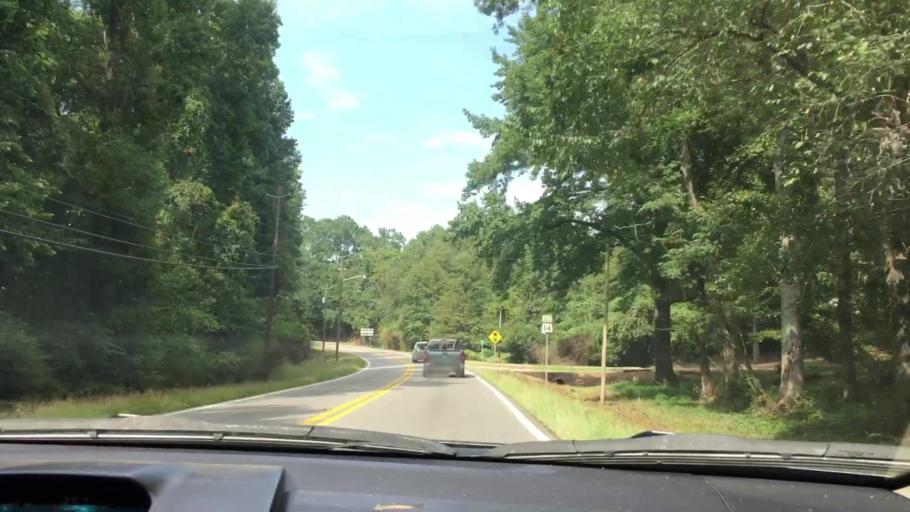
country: US
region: Alabama
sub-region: Hale County
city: Greensboro
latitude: 32.6977
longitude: -87.6019
